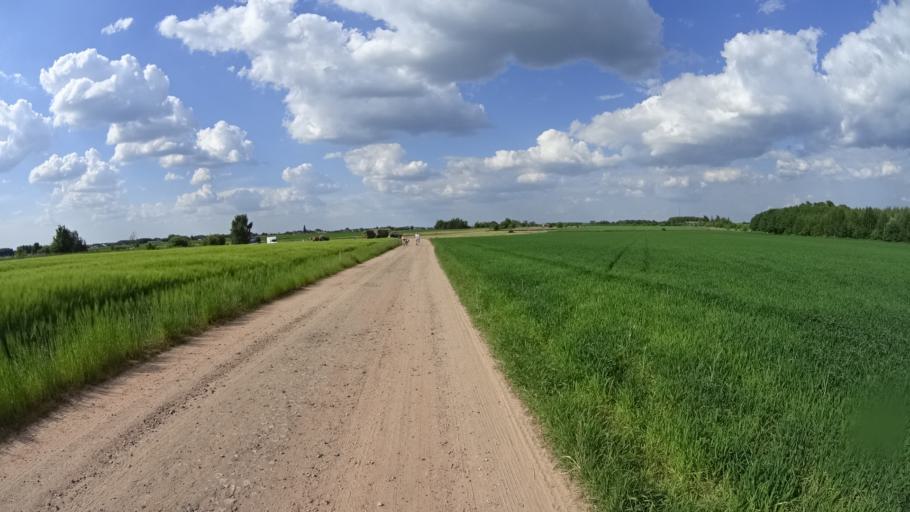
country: PL
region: Masovian Voivodeship
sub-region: Powiat piaseczynski
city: Tarczyn
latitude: 52.0200
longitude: 20.8172
